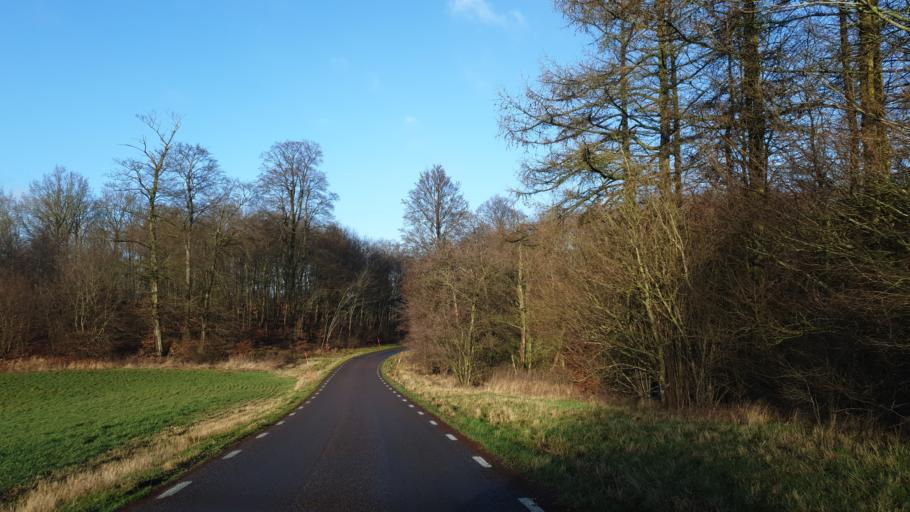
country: SE
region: Skane
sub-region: Svedala Kommun
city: Svedala
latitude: 55.4947
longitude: 13.2885
